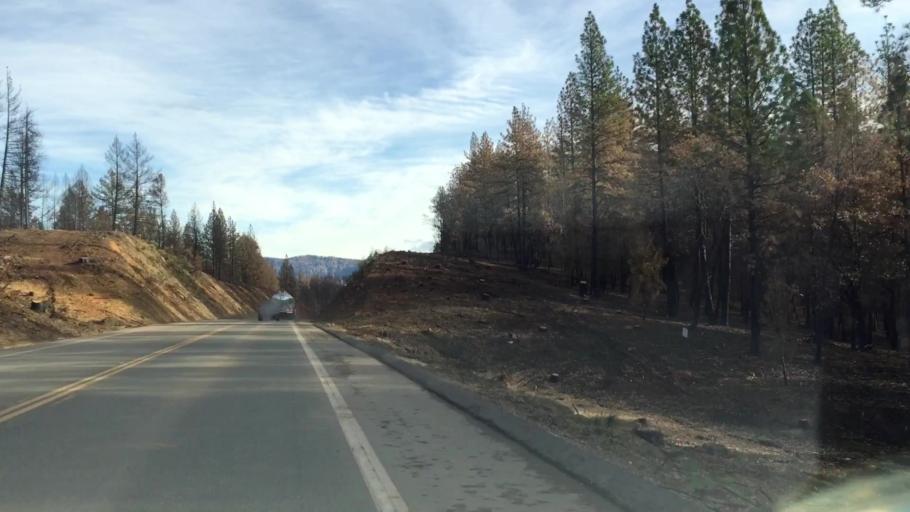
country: US
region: California
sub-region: Butte County
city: Magalia
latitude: 39.7209
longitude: -121.5144
